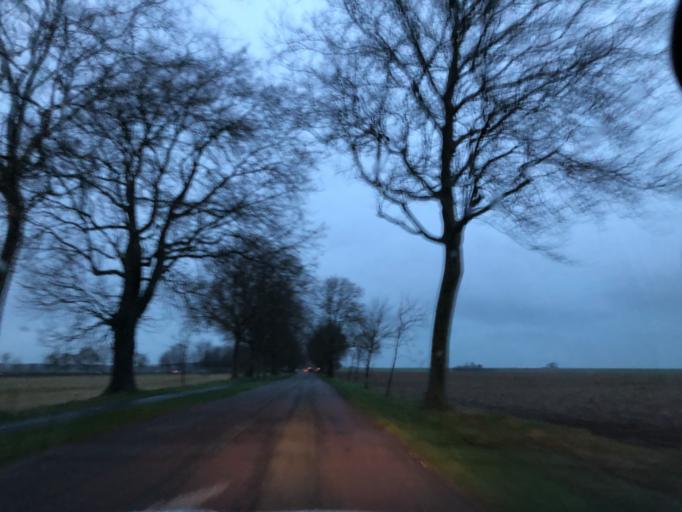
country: FR
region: Lower Normandy
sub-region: Departement du Calvados
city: Mathieu
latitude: 49.2645
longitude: -0.3757
